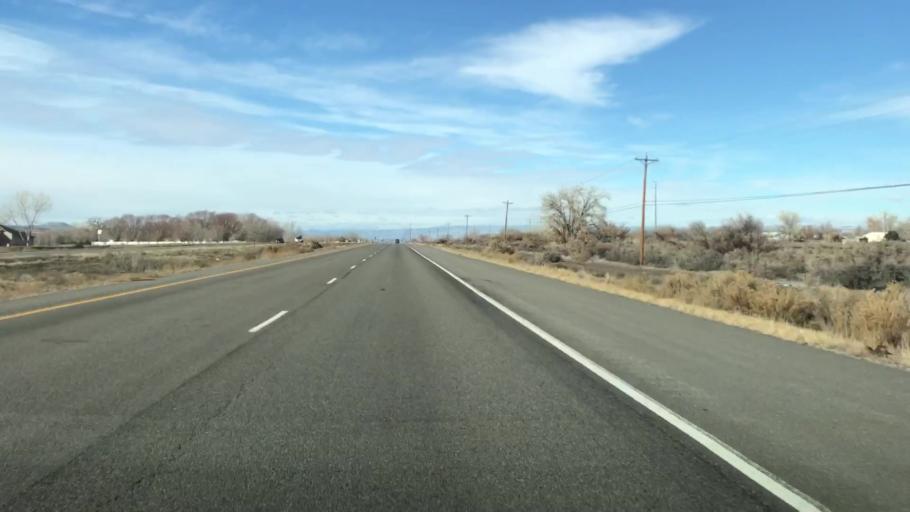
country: US
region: Colorado
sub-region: Mesa County
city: Fruita
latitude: 39.1323
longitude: -108.6904
